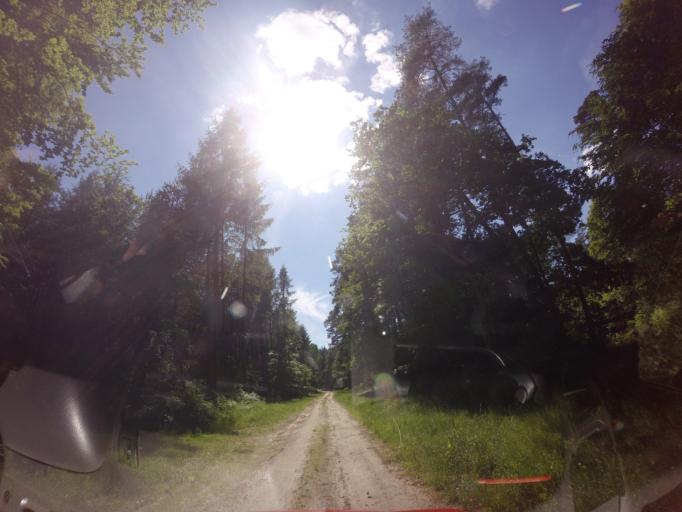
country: PL
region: West Pomeranian Voivodeship
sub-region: Powiat choszczenski
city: Drawno
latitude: 53.1667
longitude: 15.6443
